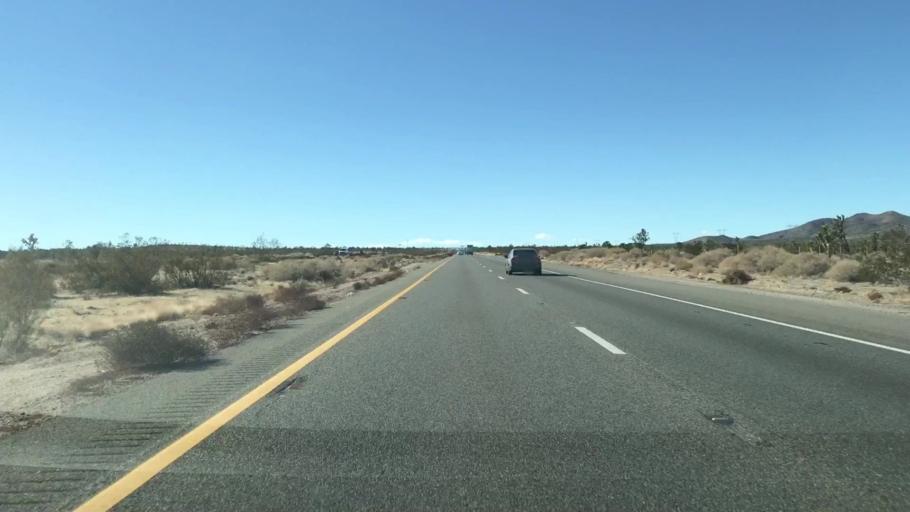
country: US
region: Nevada
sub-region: Clark County
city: Sandy Valley
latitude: 35.4133
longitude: -115.7621
